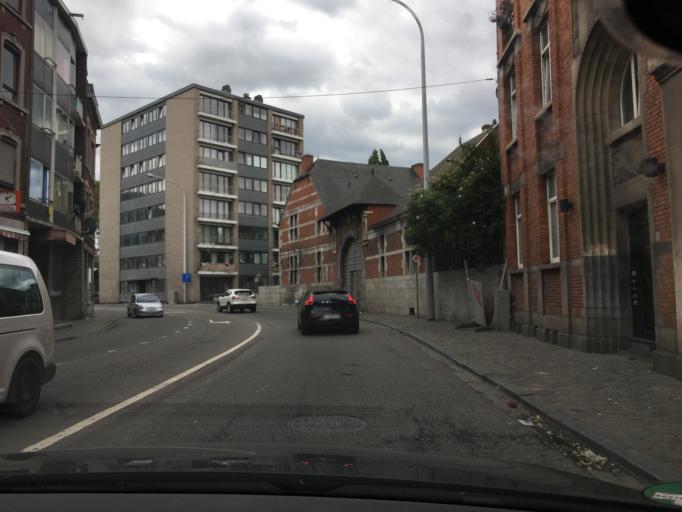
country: BE
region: Wallonia
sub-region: Province de Liege
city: Liege
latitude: 50.6361
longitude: 5.5903
